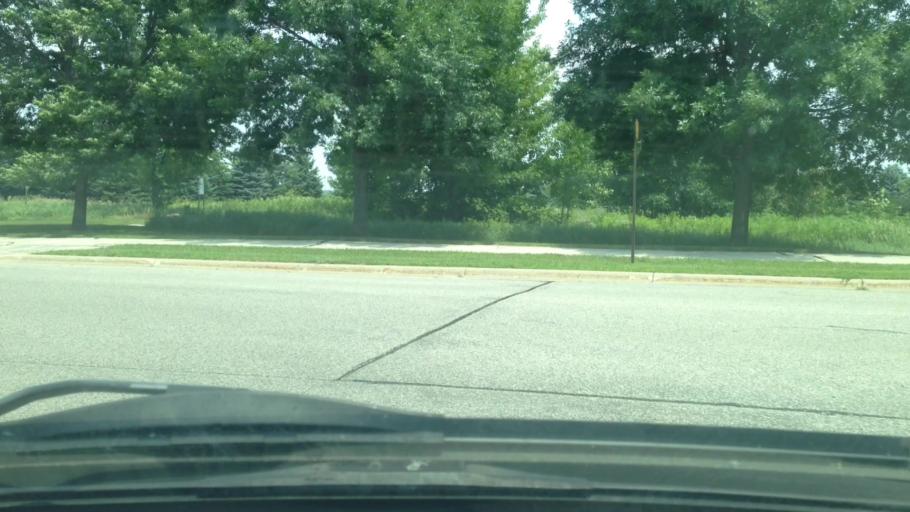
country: US
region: Minnesota
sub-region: Olmsted County
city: Rochester
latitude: 44.0604
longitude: -92.5016
